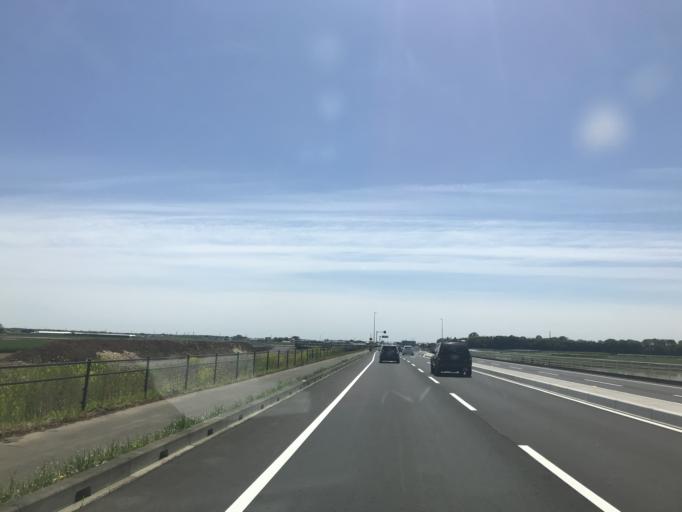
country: JP
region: Ibaraki
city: Shimodate
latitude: 36.2362
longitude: 139.9847
